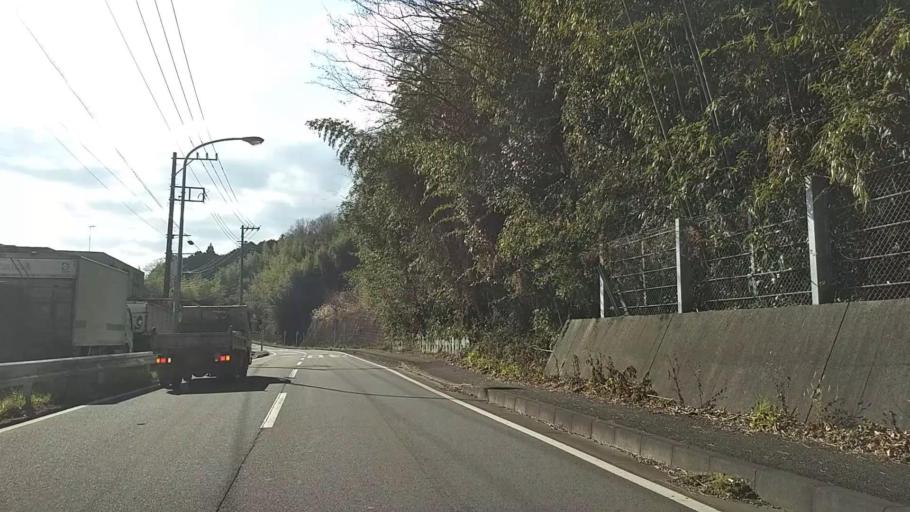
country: JP
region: Kanagawa
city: Isehara
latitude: 35.4580
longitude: 139.2914
